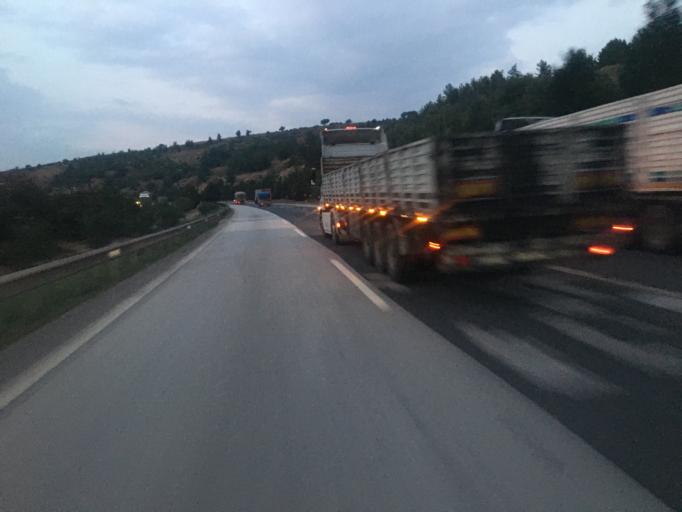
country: TR
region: Osmaniye
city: Haruniye
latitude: 37.1784
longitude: 36.3791
